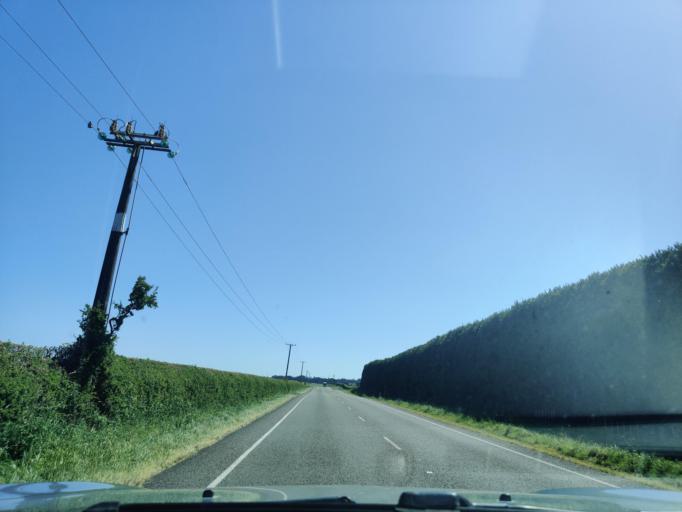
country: NZ
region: Taranaki
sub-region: South Taranaki District
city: Patea
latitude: -39.7873
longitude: 174.6997
